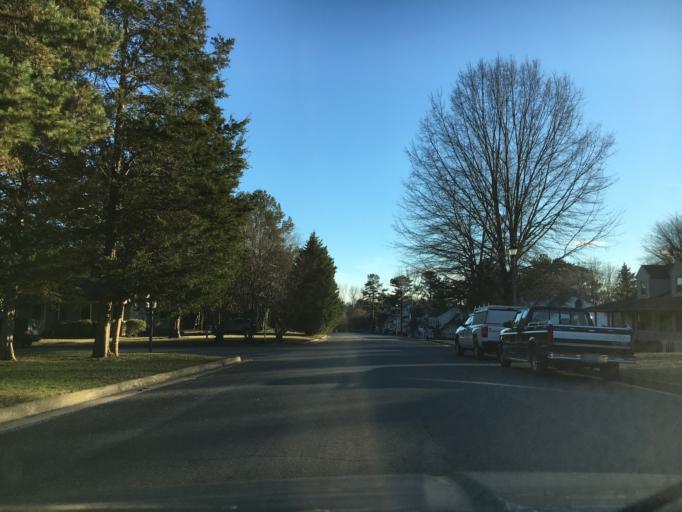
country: US
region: Virginia
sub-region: Halifax County
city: South Boston
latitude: 36.7065
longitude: -78.8847
